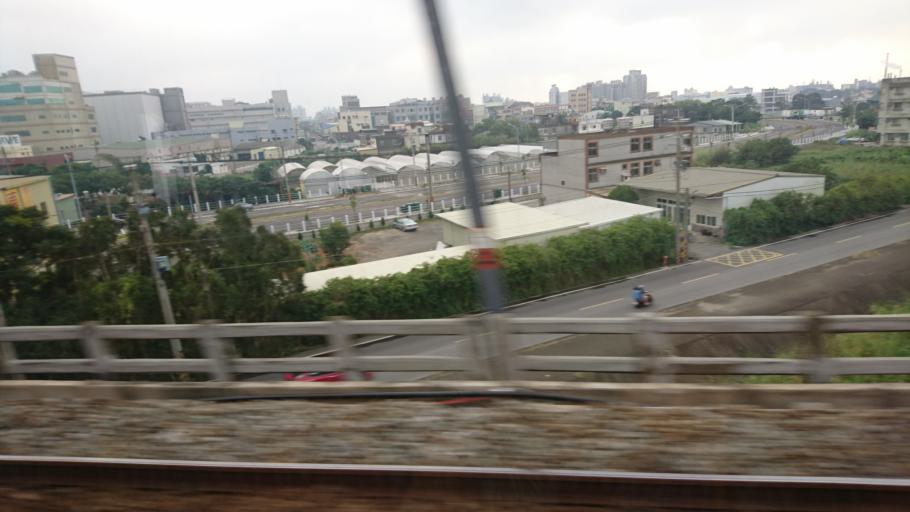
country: TW
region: Taiwan
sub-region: Hsinchu
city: Zhubei
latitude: 24.8510
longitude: 121.0130
